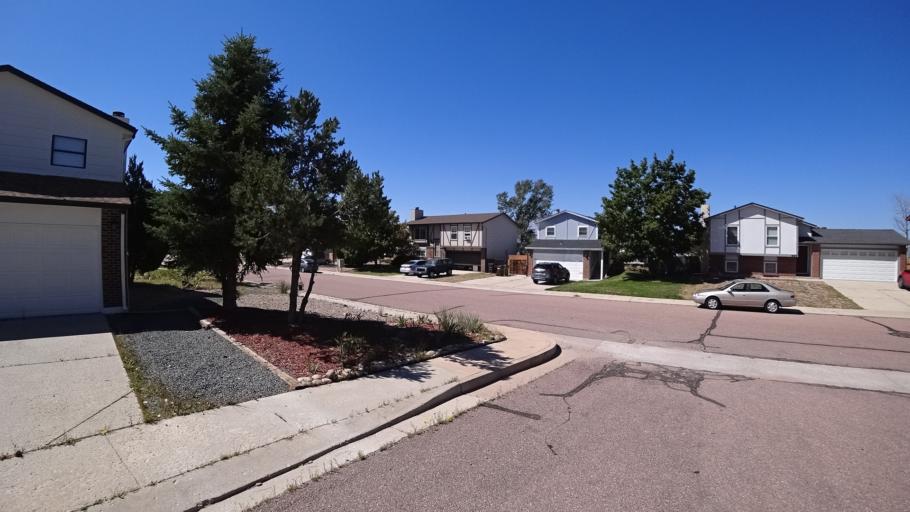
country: US
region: Colorado
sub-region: El Paso County
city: Black Forest
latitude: 38.9501
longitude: -104.7559
